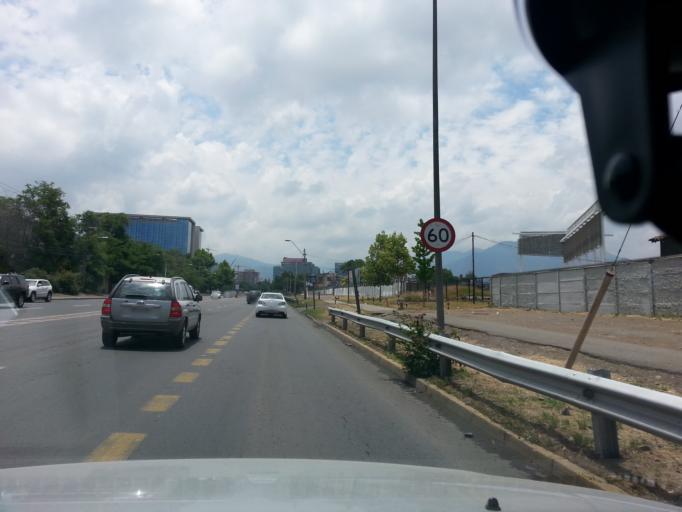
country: CL
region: Santiago Metropolitan
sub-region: Provincia de Santiago
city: Villa Presidente Frei, Nunoa, Santiago, Chile
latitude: -33.3819
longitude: -70.5319
